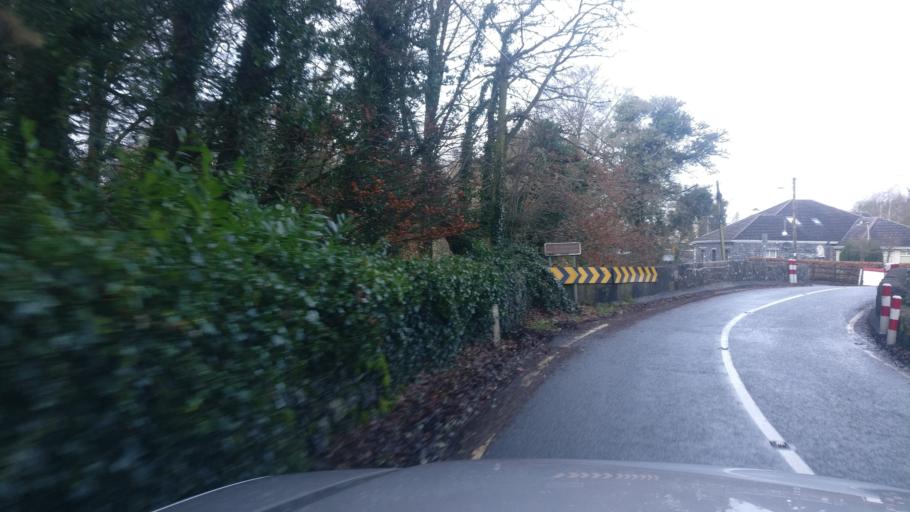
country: IE
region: Connaught
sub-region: County Galway
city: Loughrea
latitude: 53.2839
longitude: -8.5873
